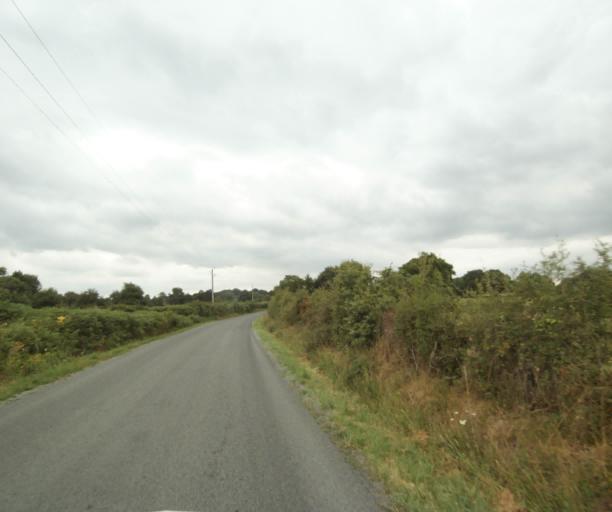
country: FR
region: Pays de la Loire
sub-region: Departement de la Sarthe
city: Sable-sur-Sarthe
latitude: 47.8163
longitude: -0.3405
